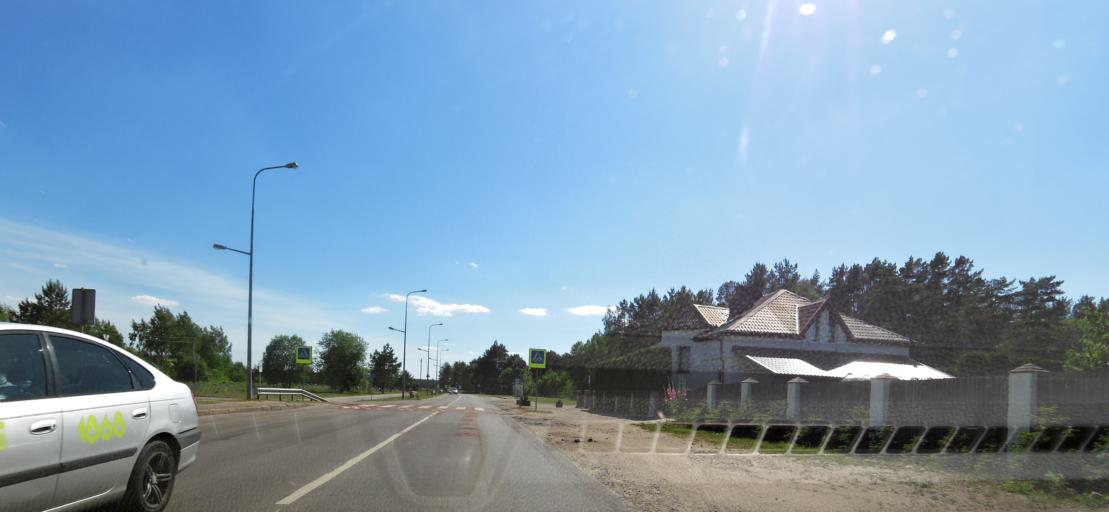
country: LT
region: Vilnius County
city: Rasos
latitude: 54.7810
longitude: 25.3427
